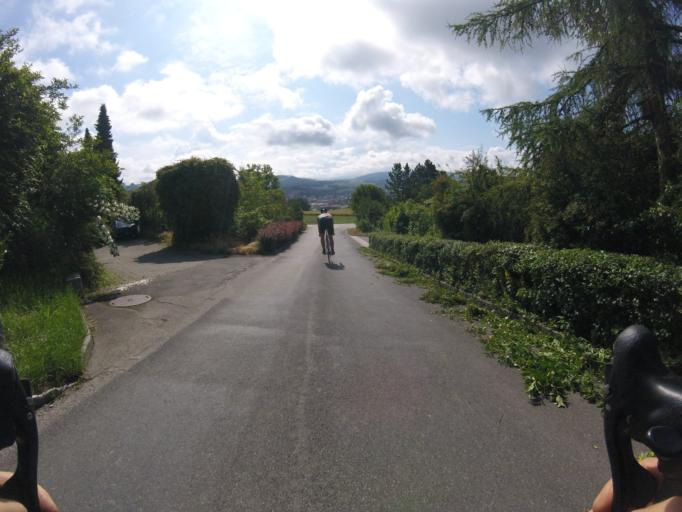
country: CH
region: Bern
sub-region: Bern-Mittelland District
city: Worb
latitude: 46.9350
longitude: 7.5436
